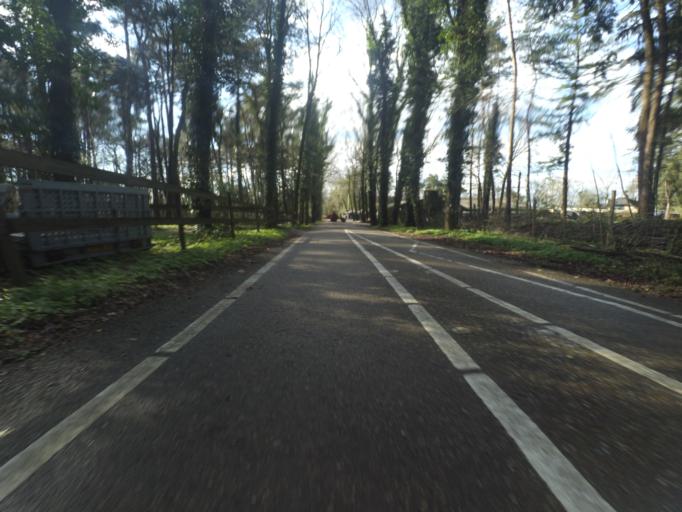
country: NL
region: Gelderland
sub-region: Gemeente Apeldoorn
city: Beekbergen
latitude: 52.1685
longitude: 5.9516
